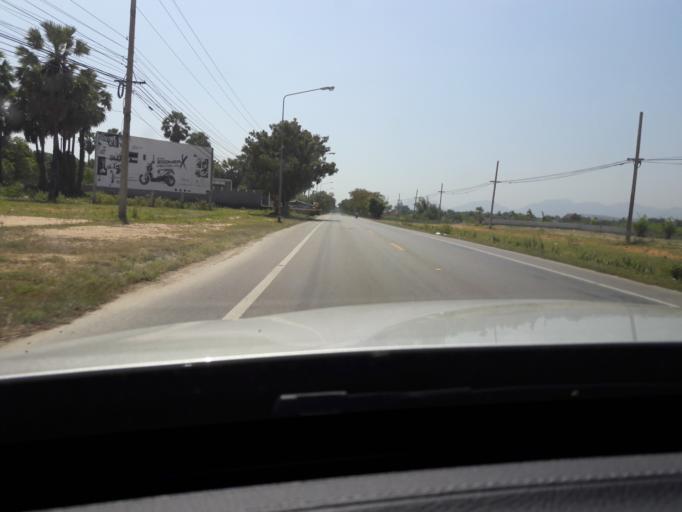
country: TH
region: Phetchaburi
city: Cha-am
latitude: 12.8300
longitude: 99.9877
